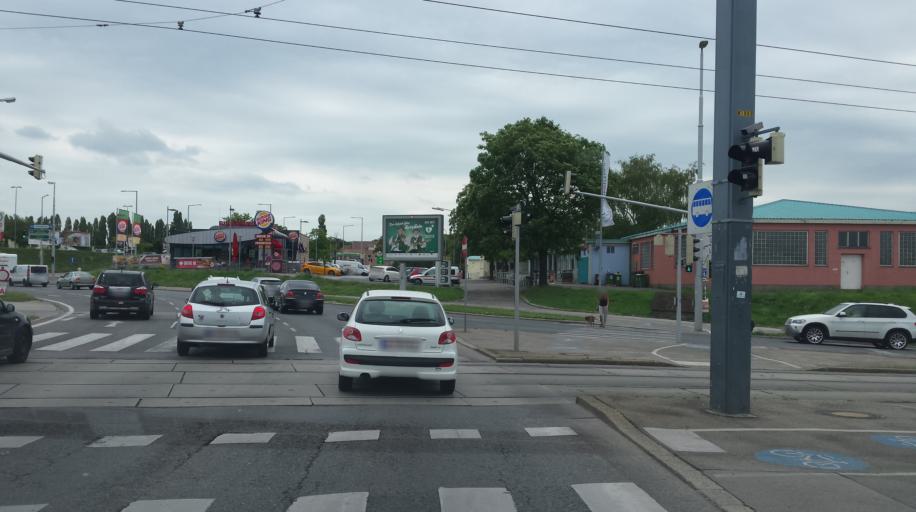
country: AT
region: Lower Austria
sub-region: Politischer Bezirk Wien-Umgebung
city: Leopoldsdorf
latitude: 48.1599
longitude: 16.3832
